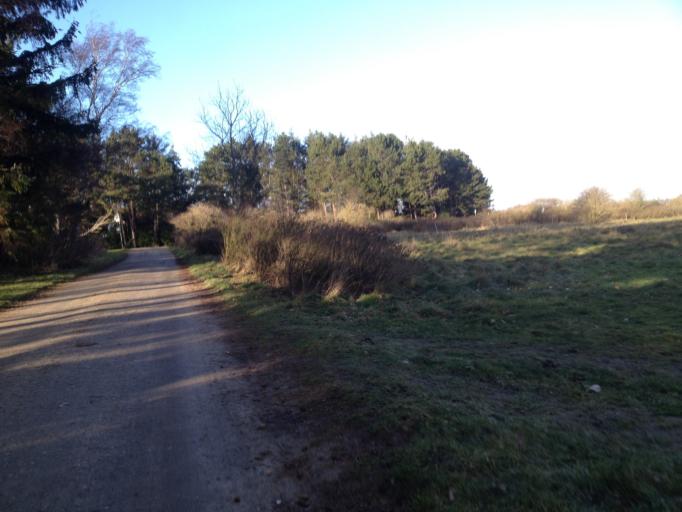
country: DE
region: Schleswig-Holstein
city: Nebel
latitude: 54.6454
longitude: 8.3471
